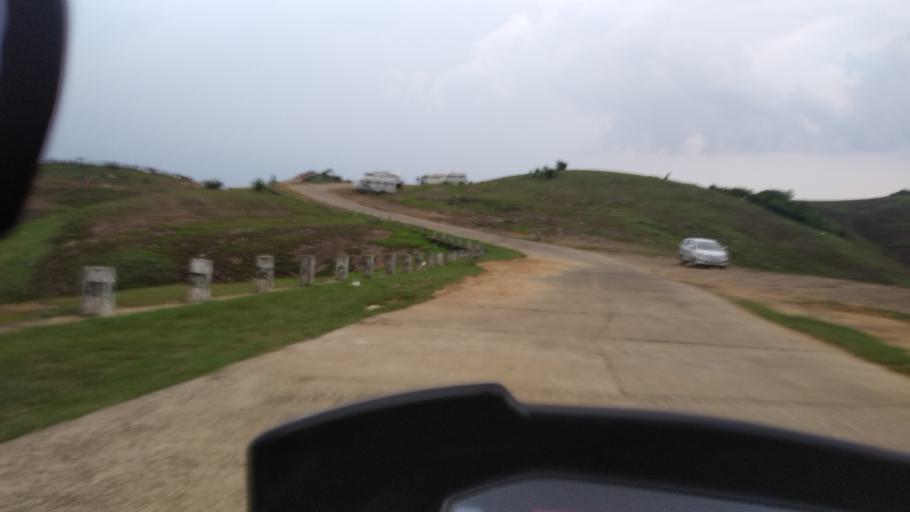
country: IN
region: Tamil Nadu
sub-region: Theni
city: Gudalur
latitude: 9.5493
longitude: 77.0330
